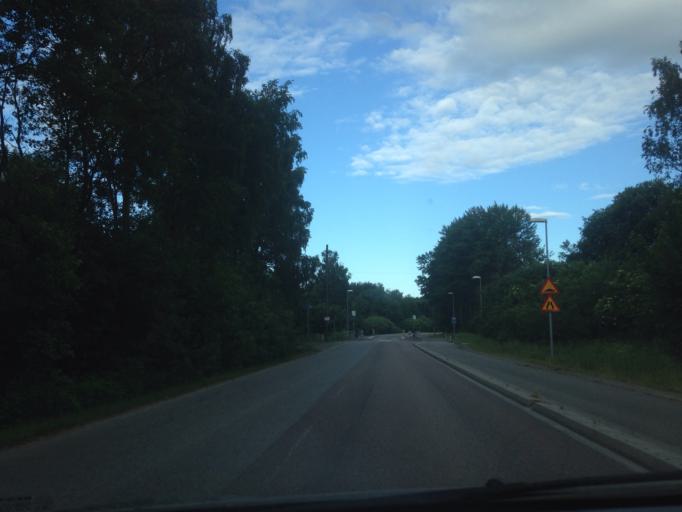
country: SE
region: Vaestra Goetaland
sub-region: Goteborg
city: Torslanda
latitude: 57.7637
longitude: 11.8223
